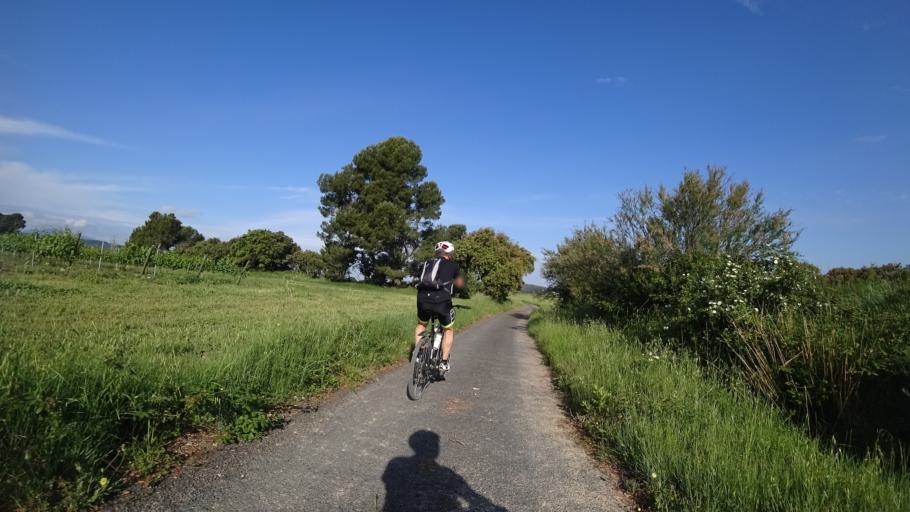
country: FR
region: Languedoc-Roussillon
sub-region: Departement de l'Herault
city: Olonzac
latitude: 43.2381
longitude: 2.7372
